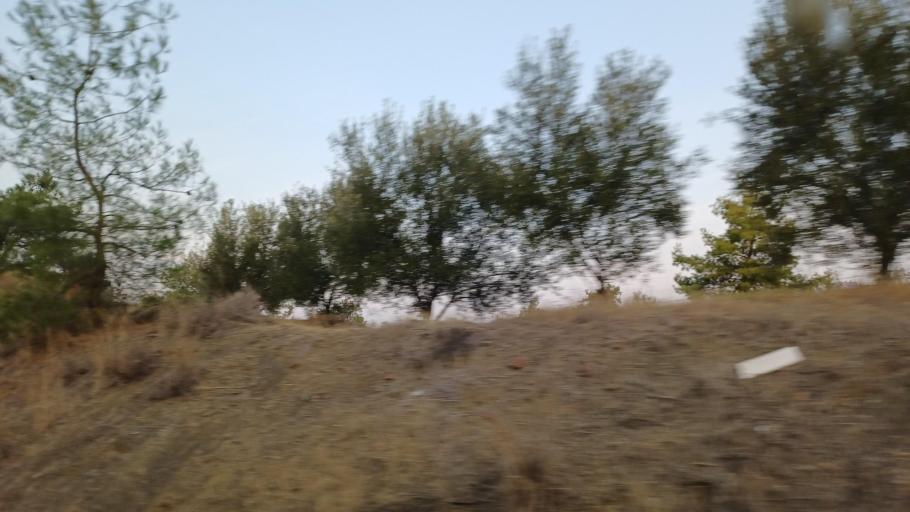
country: CY
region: Larnaka
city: Kornos
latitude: 34.9168
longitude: 33.3818
